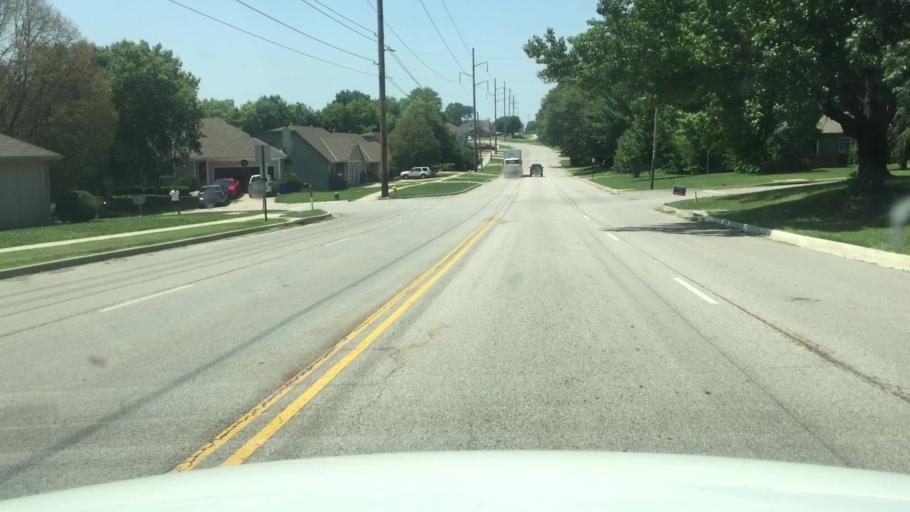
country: US
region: Missouri
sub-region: Jackson County
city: Grandview
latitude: 38.8731
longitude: -94.5385
